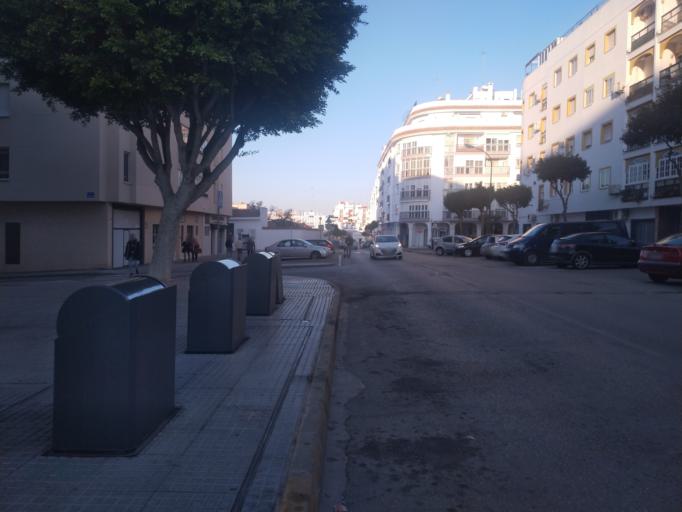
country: ES
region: Andalusia
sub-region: Provincia de Cadiz
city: San Fernando
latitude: 36.4624
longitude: -6.2017
